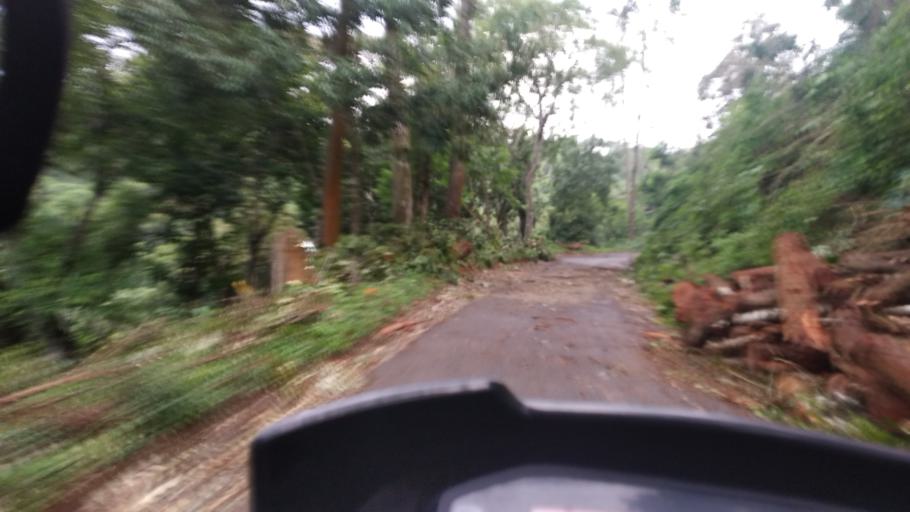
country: IN
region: Tamil Nadu
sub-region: Theni
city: Gudalur
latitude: 9.5514
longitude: 77.0604
